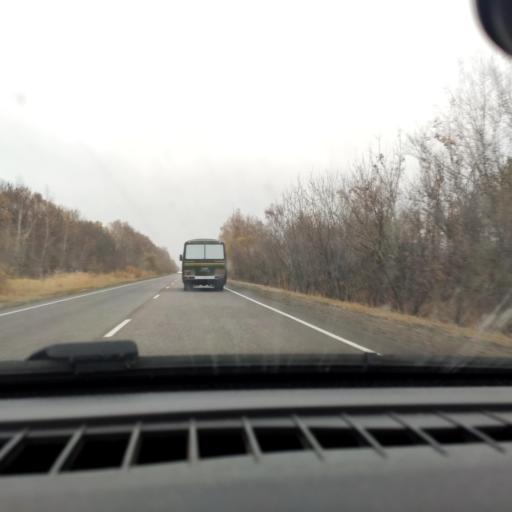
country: RU
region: Voronezj
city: Kolodeznyy
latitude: 51.3538
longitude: 39.0237
